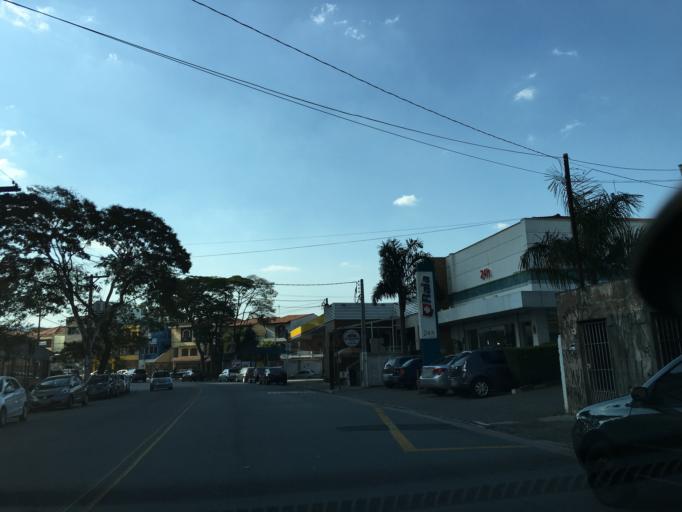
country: BR
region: Sao Paulo
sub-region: Sao Paulo
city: Sao Paulo
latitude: -23.4717
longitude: -46.6299
